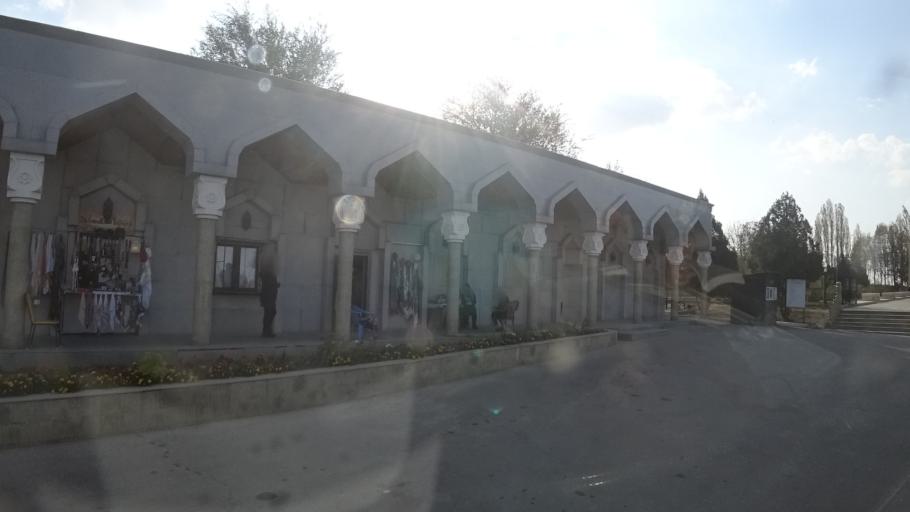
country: KZ
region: Zhambyl
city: Taraz
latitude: 42.8338
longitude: 71.2117
